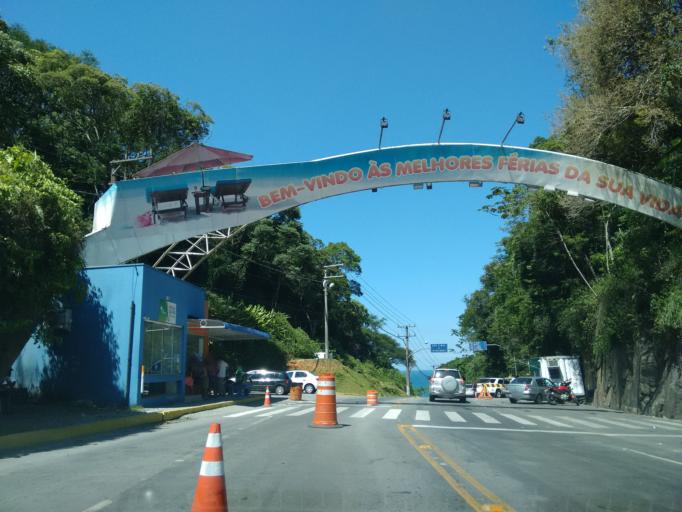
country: BR
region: Santa Catarina
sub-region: Porto Belo
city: Porto Belo
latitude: -27.1385
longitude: -48.5230
